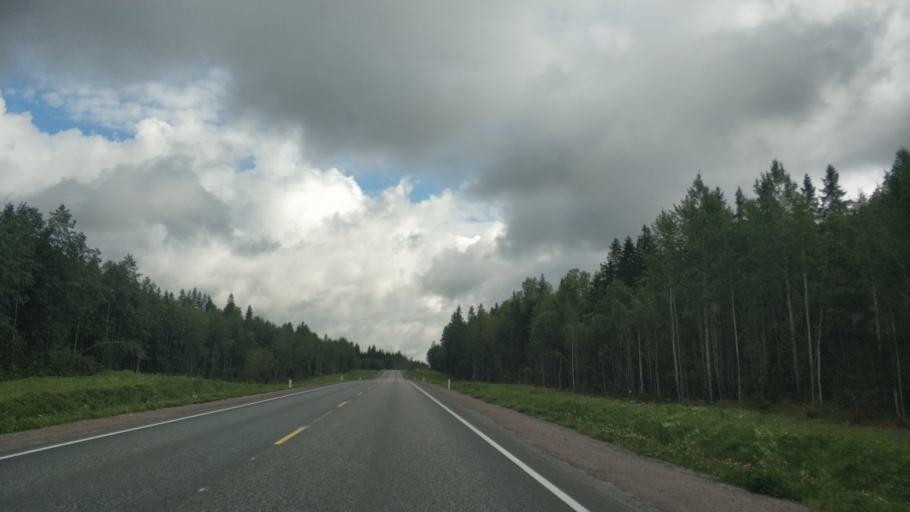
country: RU
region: Republic of Karelia
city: Ruskeala
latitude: 61.8568
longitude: 30.6519
